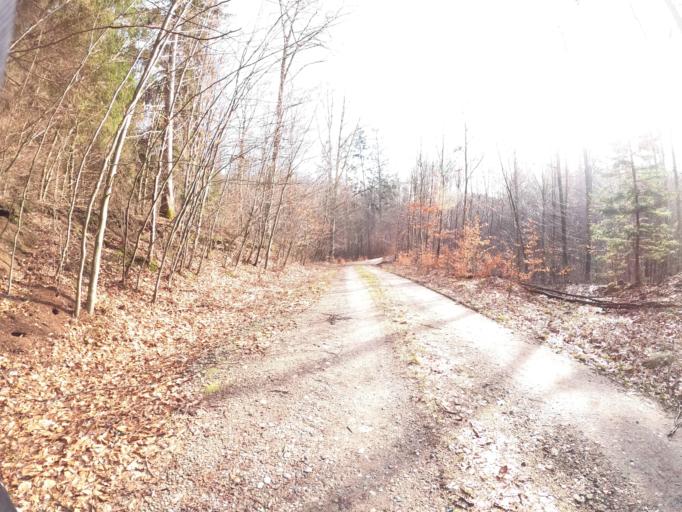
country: PL
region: West Pomeranian Voivodeship
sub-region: Powiat koszalinski
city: Polanow
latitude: 54.2270
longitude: 16.6399
